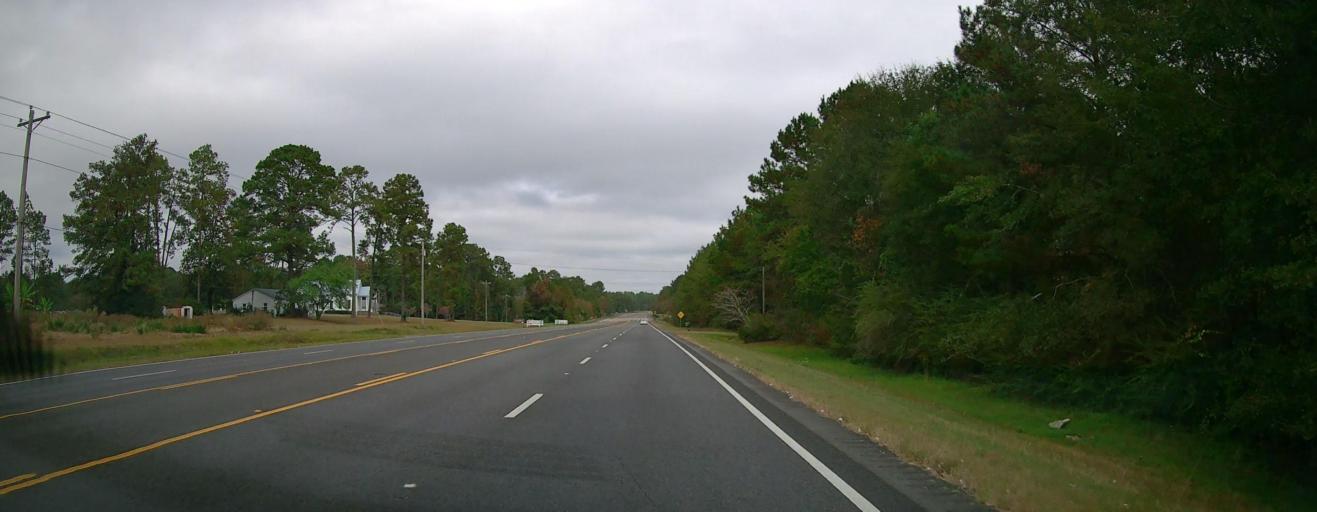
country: US
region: Georgia
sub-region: Thomas County
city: Thomasville
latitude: 30.9708
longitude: -83.8904
